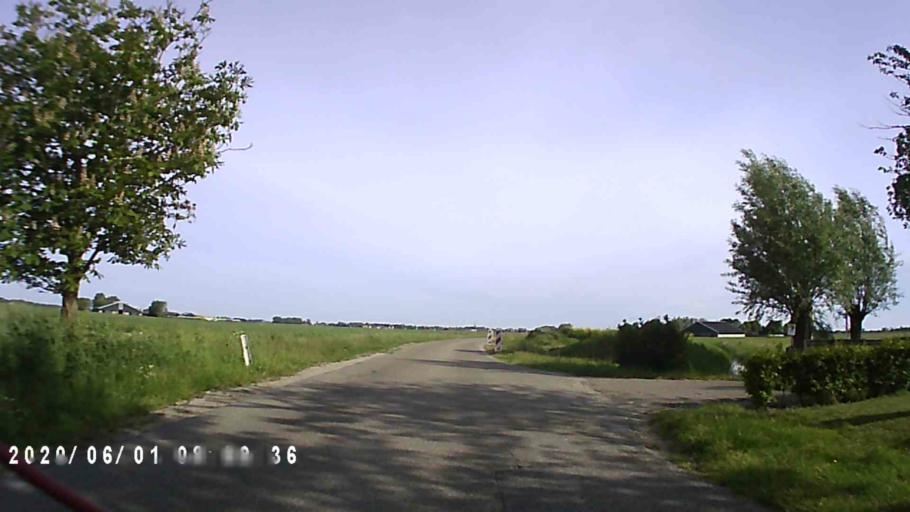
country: NL
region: Friesland
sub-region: Gemeente Ferwerderadiel
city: Hallum
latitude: 53.2838
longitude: 5.7977
